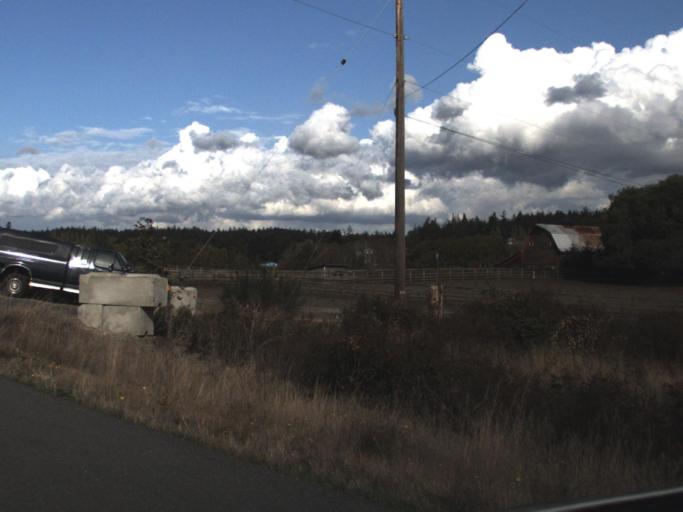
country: US
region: Washington
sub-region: Island County
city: Coupeville
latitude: 48.2419
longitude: -122.7141
